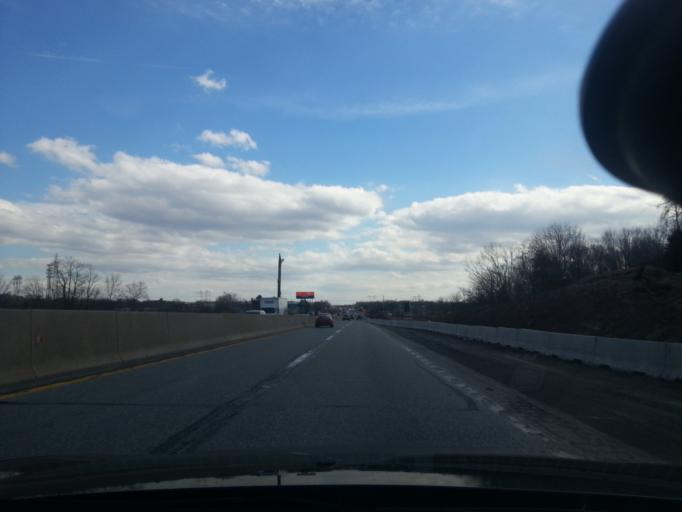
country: US
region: Pennsylvania
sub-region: Montgomery County
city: Kulpsville
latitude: 40.2645
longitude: -75.3540
